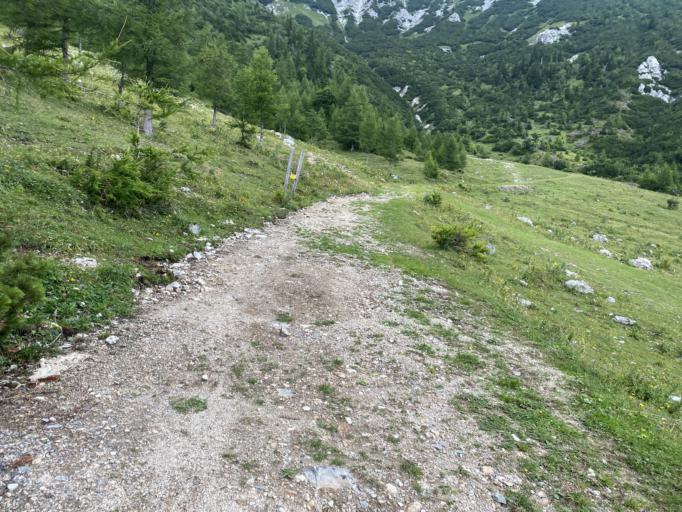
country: AT
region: Styria
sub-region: Politischer Bezirk Bruck-Muerzzuschlag
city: Spital am Semmering
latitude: 47.6887
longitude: 15.7131
